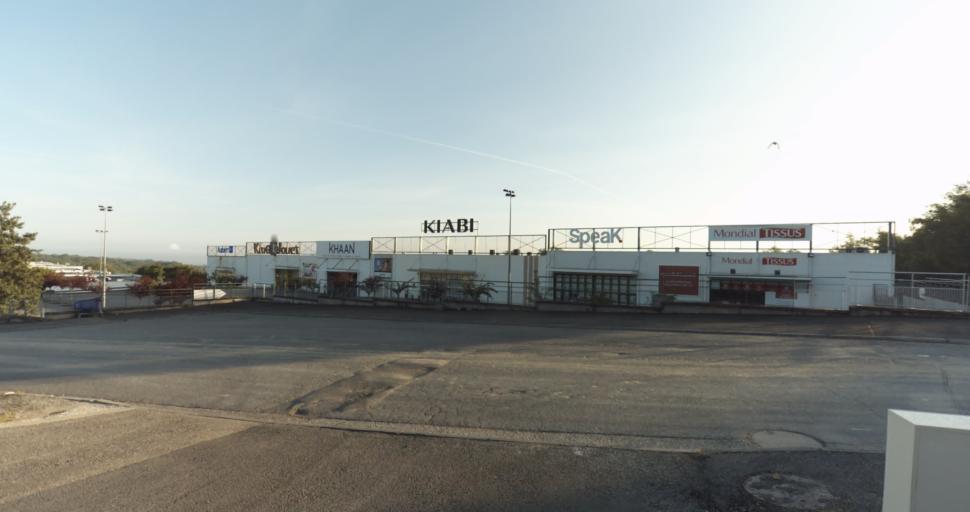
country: FR
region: Limousin
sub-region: Departement de la Haute-Vienne
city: Boisseuil
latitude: 45.7796
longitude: 1.3112
